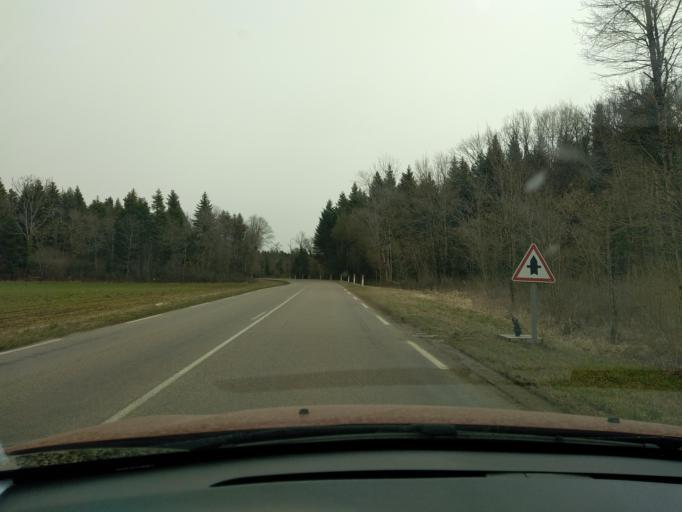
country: FR
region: Franche-Comte
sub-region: Departement du Jura
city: Champagnole
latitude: 46.7516
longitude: 5.8385
